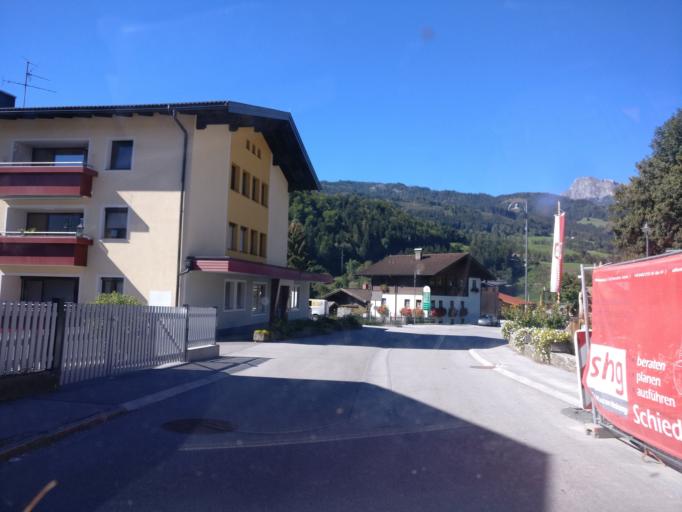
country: AT
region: Salzburg
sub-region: Politischer Bezirk Sankt Johann im Pongau
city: Pfarrwerfen
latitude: 47.4572
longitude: 13.2048
